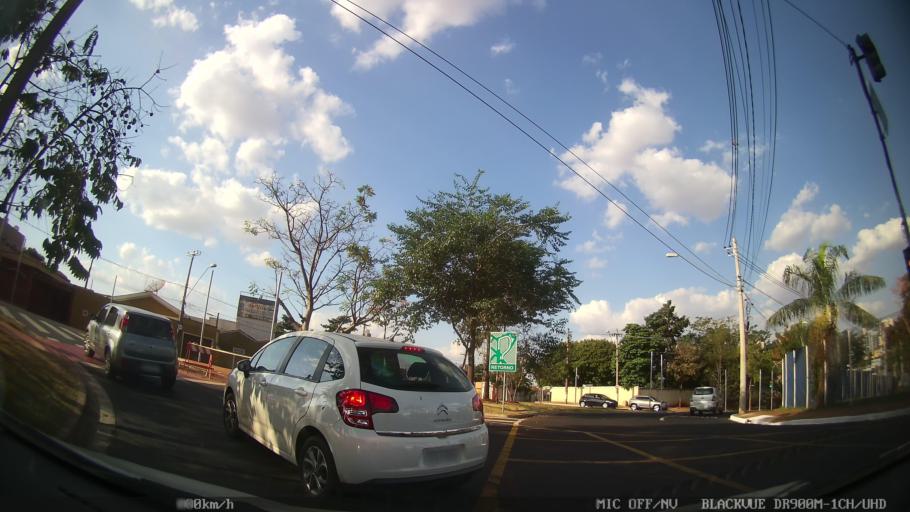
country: BR
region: Sao Paulo
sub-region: Ribeirao Preto
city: Ribeirao Preto
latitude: -21.1745
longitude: -47.8179
